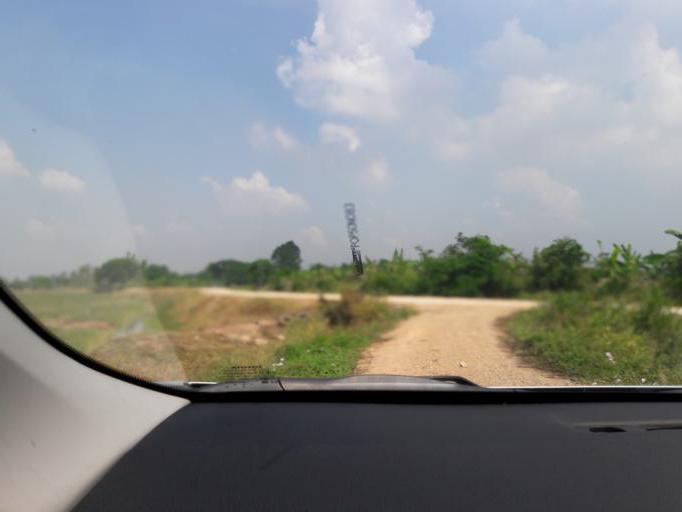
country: TH
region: Ang Thong
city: Ang Thong
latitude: 14.5626
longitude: 100.4148
